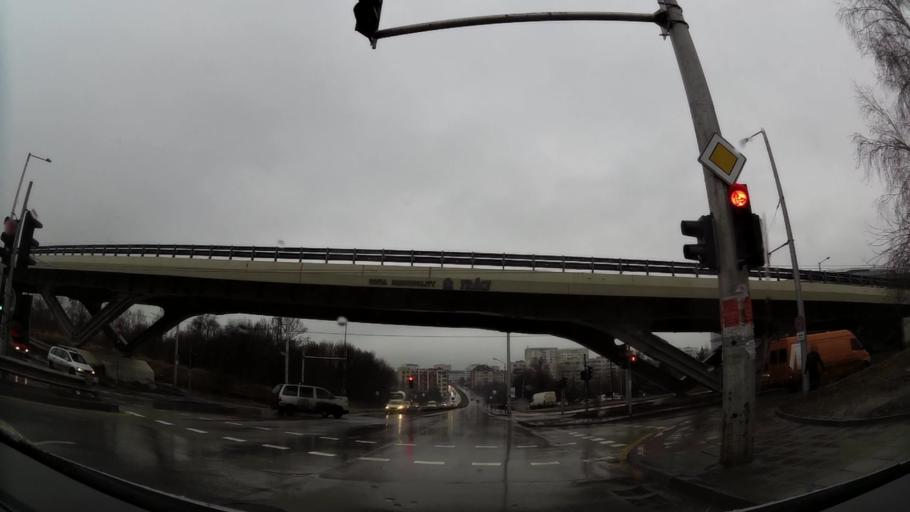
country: BG
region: Sofia-Capital
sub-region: Stolichna Obshtina
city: Sofia
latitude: 42.6498
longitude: 23.3681
